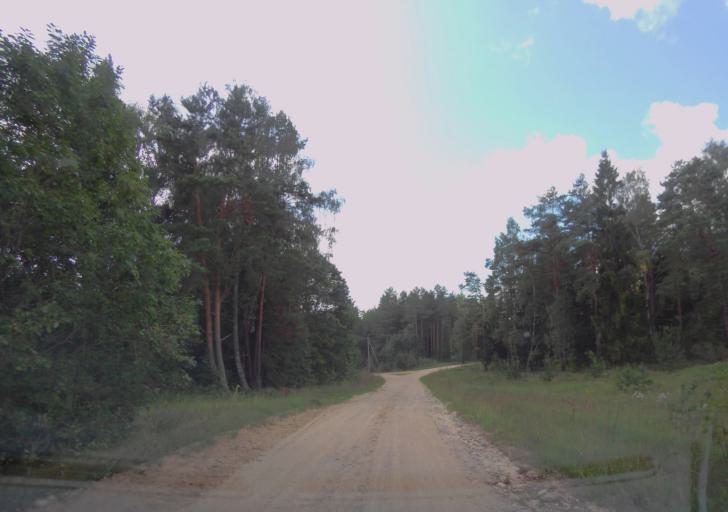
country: BY
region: Minsk
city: Horad Barysaw
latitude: 54.4241
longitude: 28.4672
